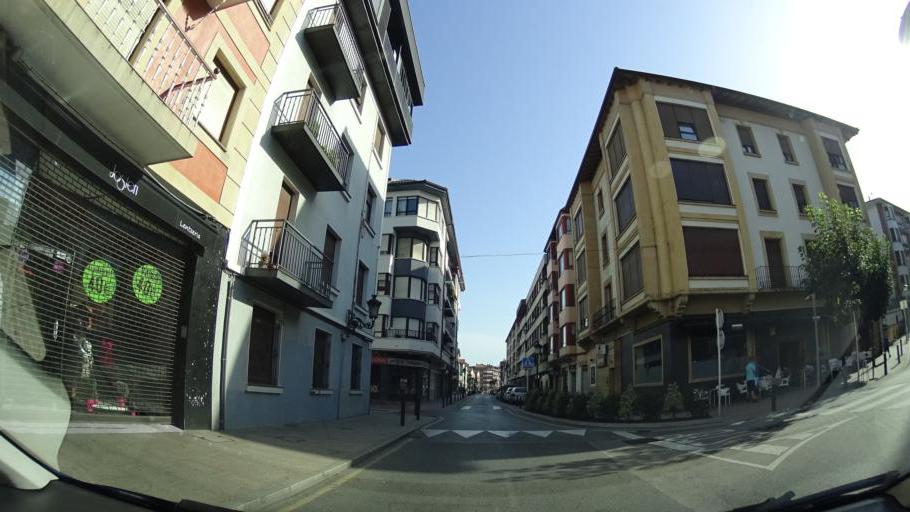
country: ES
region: Basque Country
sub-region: Bizkaia
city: Gernika-Lumo
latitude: 43.3115
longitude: -2.6788
